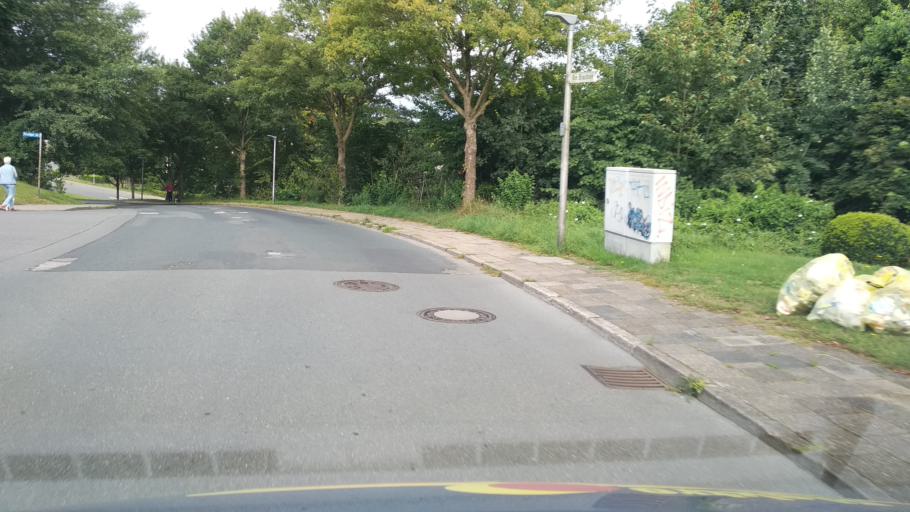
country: DE
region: Schleswig-Holstein
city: Schleswig
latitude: 54.5252
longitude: 9.5739
